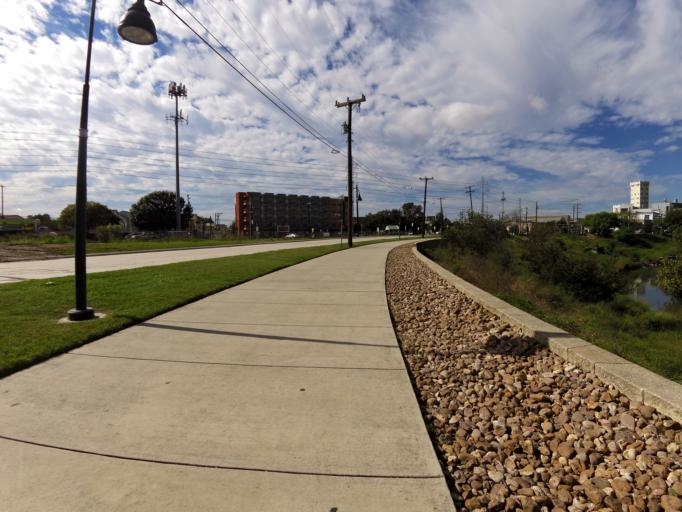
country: US
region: Texas
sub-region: Bexar County
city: San Antonio
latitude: 29.4067
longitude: -98.4942
